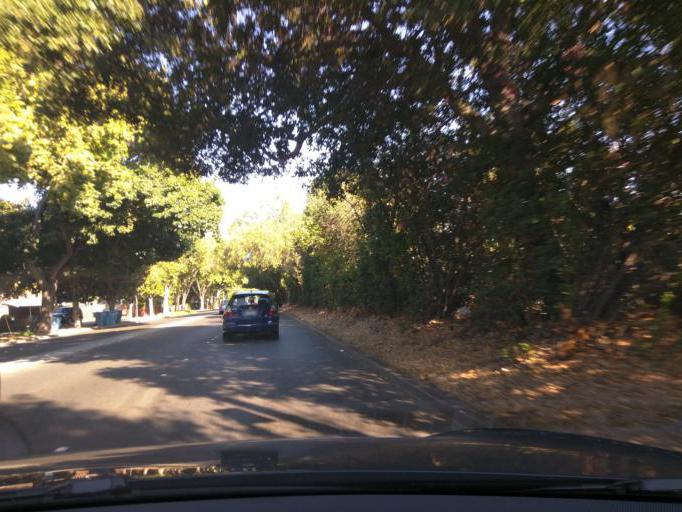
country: US
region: California
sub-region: Santa Clara County
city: Palo Alto
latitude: 37.4347
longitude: -122.1502
